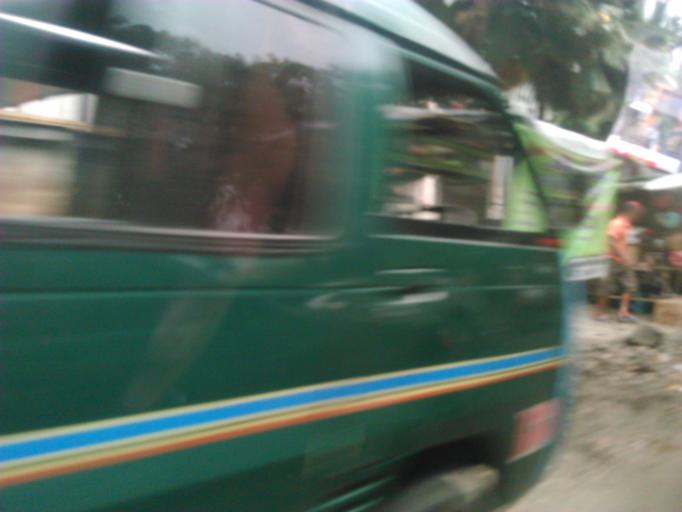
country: ID
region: East Java
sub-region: Kota Surabaya
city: Surabaya
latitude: -7.2484
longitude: 112.7327
